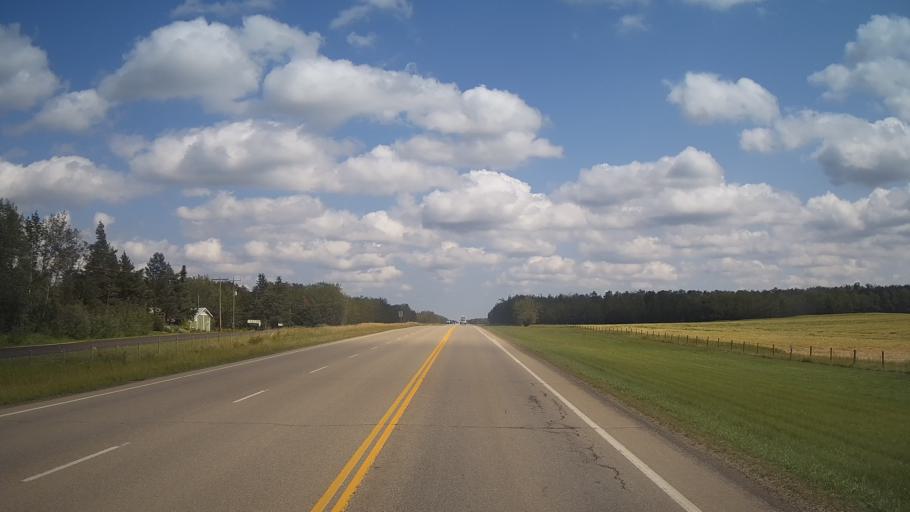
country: CA
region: Alberta
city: Sherwood Park
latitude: 53.3957
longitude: -113.0609
